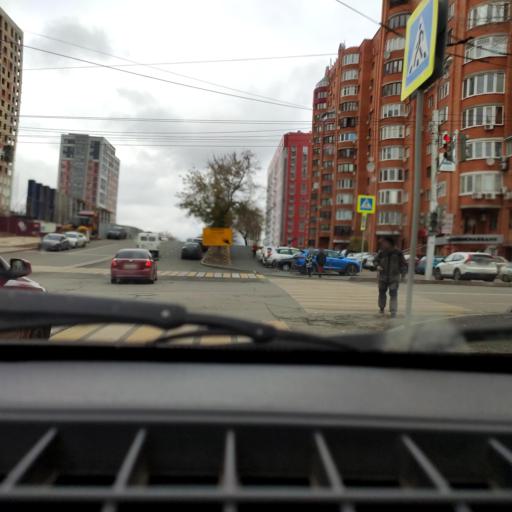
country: RU
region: Bashkortostan
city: Ufa
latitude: 54.7289
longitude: 55.9297
